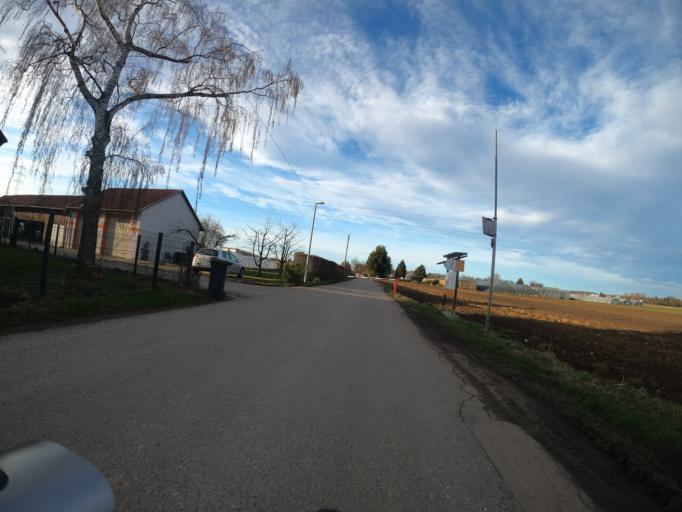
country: DE
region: Baden-Wuerttemberg
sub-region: Regierungsbezirk Stuttgart
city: Denkendorf
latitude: 48.7072
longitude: 9.3162
